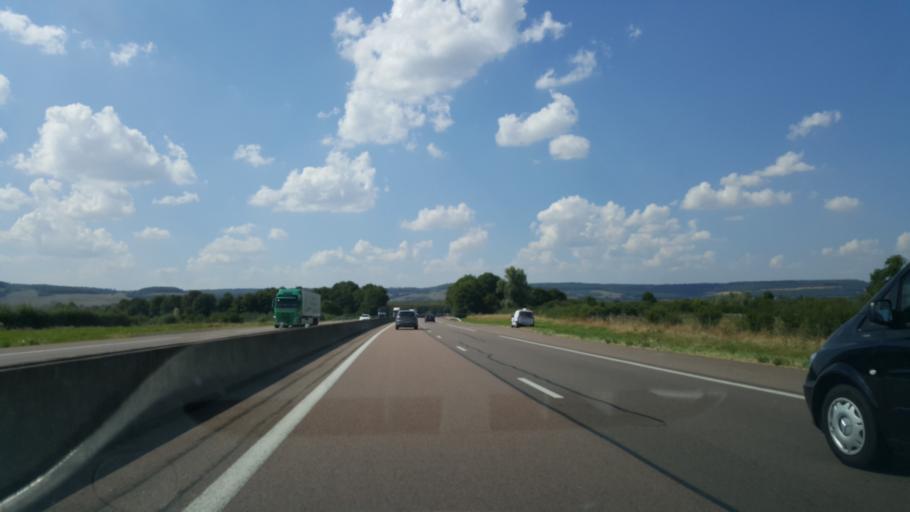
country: FR
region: Bourgogne
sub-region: Departement de la Cote-d'Or
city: Pouilly-en-Auxois
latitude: 47.2577
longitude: 4.5304
